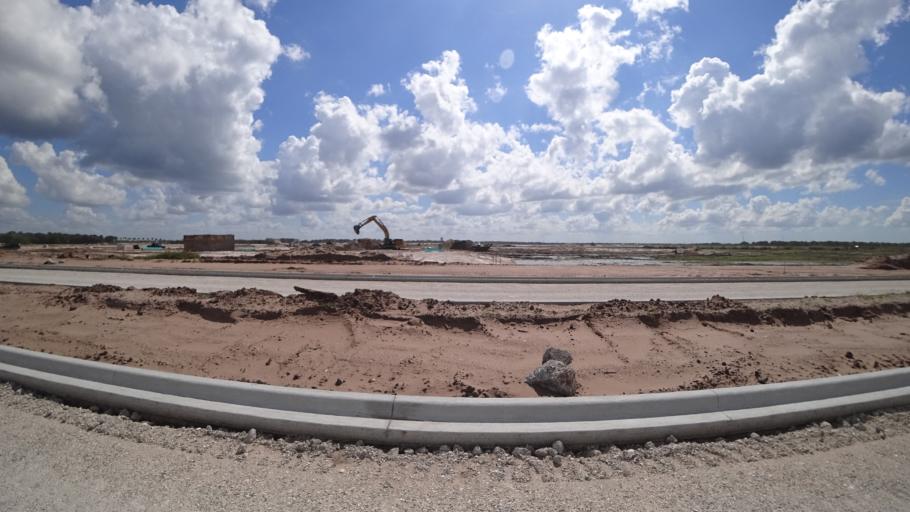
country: US
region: Florida
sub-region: Sarasota County
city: The Meadows
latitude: 27.4541
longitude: -82.3802
